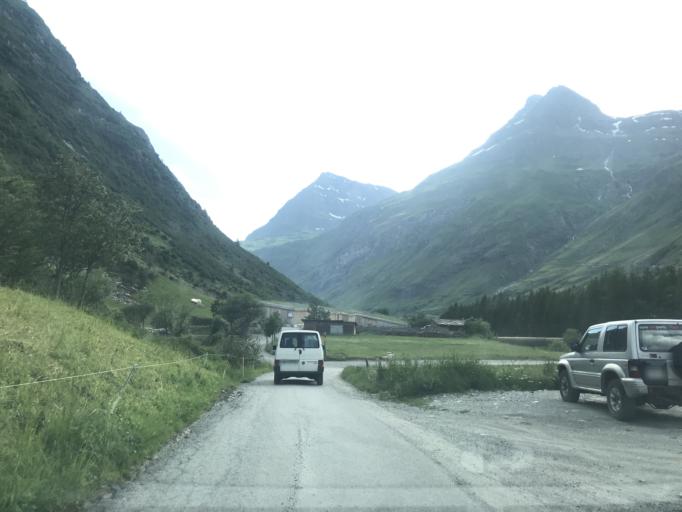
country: FR
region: Rhone-Alpes
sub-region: Departement de la Savoie
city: Val-d'Isere
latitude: 45.3731
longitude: 7.0546
